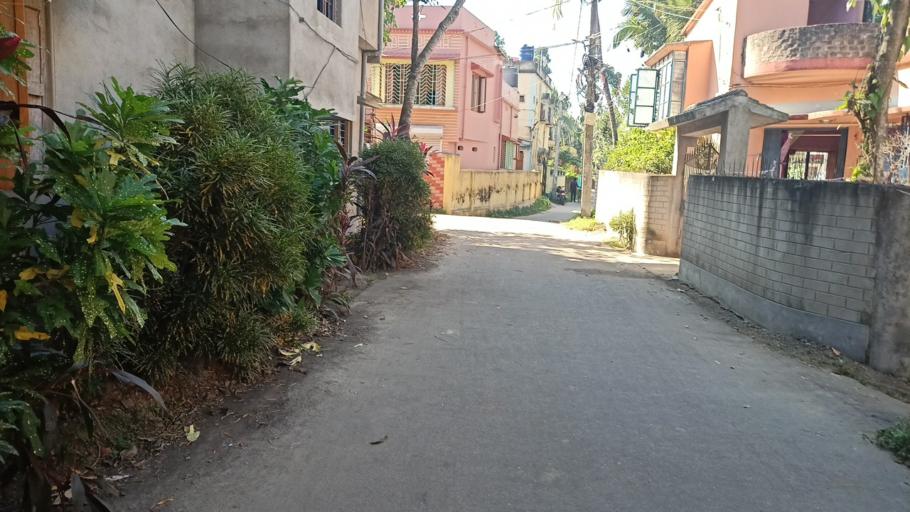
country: IN
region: West Bengal
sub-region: North 24 Parganas
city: Bangaon
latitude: 23.0529
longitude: 88.8245
